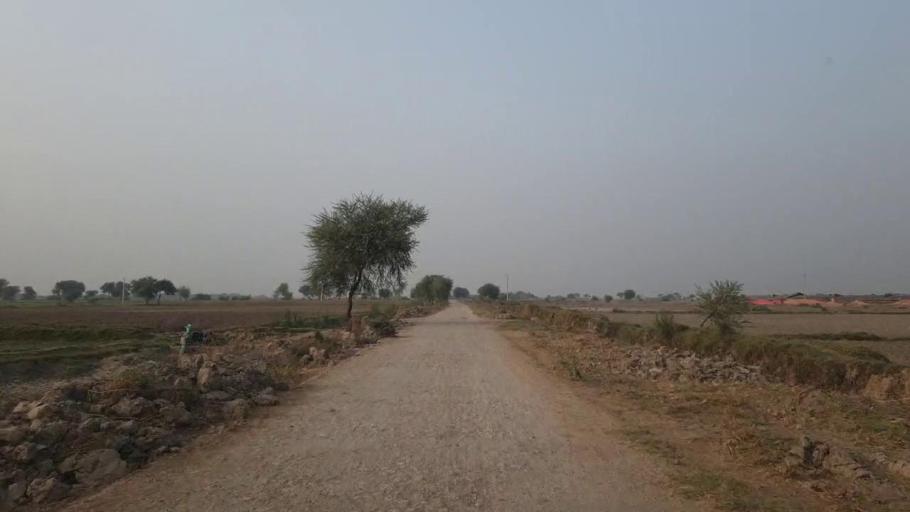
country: PK
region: Sindh
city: Mirpur Batoro
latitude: 24.6573
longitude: 68.3785
